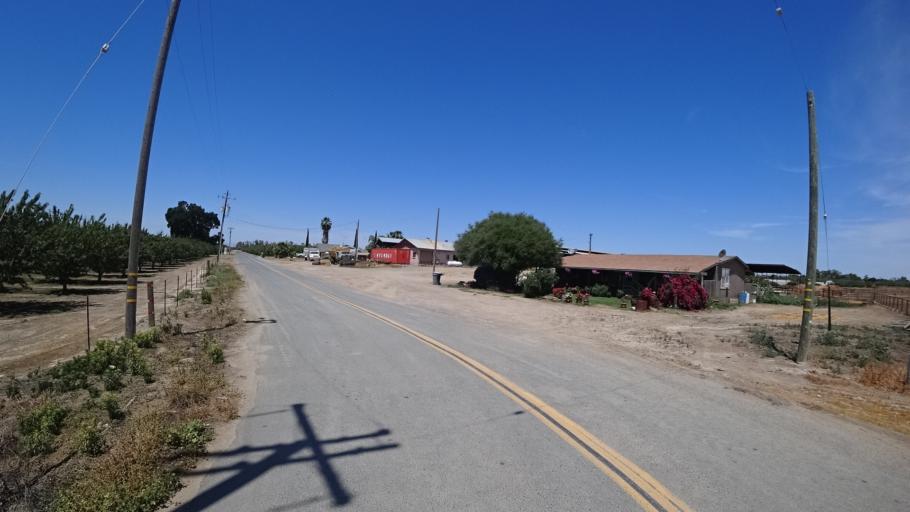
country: US
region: California
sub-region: Kings County
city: Lemoore
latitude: 36.3570
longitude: -119.7991
